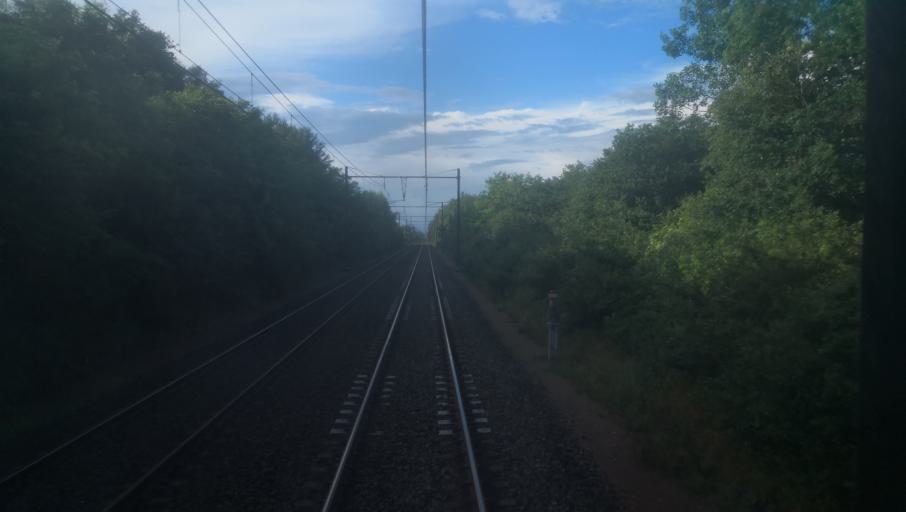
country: FR
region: Centre
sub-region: Departement du Loir-et-Cher
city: Salbris
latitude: 47.4603
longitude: 2.0411
